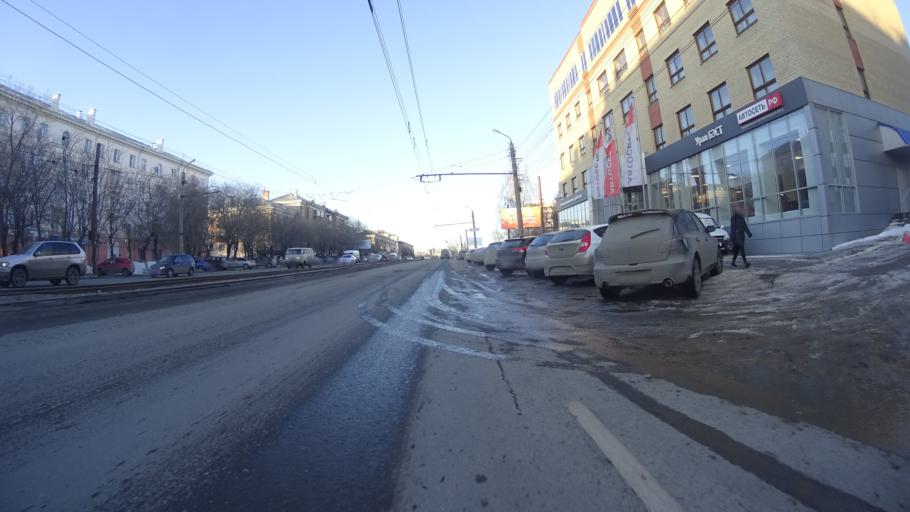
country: RU
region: Chelyabinsk
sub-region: Gorod Chelyabinsk
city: Chelyabinsk
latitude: 55.1424
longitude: 61.4431
